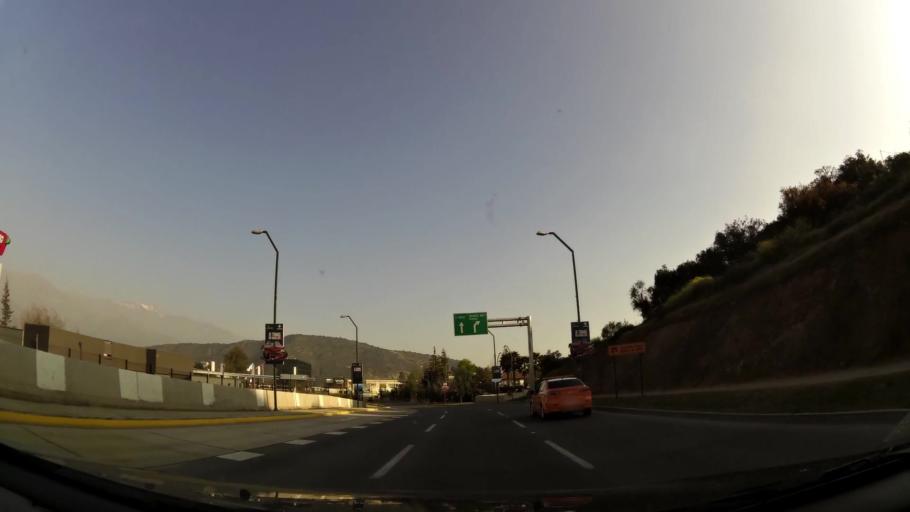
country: CL
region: Santiago Metropolitan
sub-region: Provincia de Santiago
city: Villa Presidente Frei, Nunoa, Santiago, Chile
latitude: -33.3534
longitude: -70.5404
